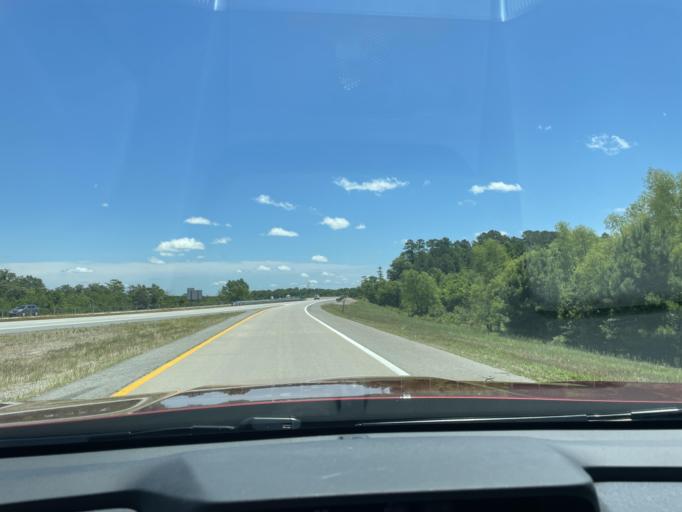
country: US
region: Arkansas
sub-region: Jefferson County
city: Pine Bluff
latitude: 34.1707
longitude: -92.0041
